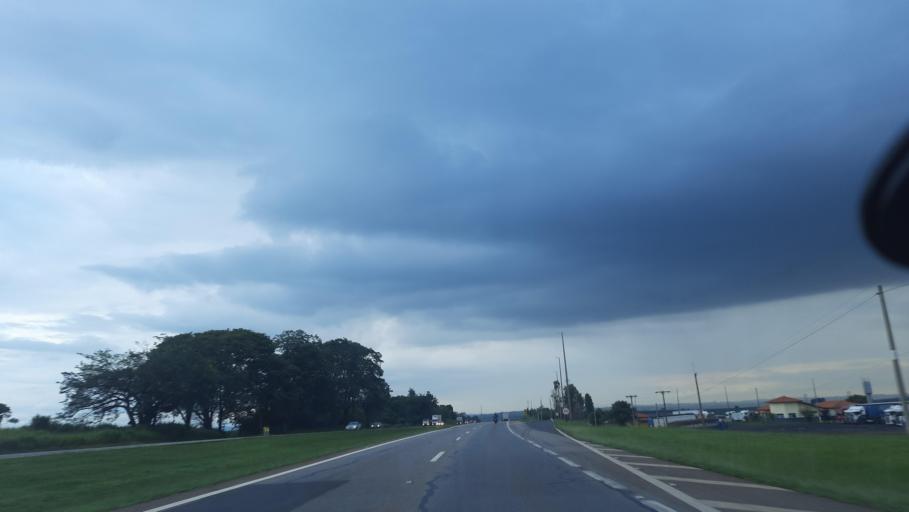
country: BR
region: Sao Paulo
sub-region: Mogi-Mirim
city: Mogi Mirim
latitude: -22.5243
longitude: -46.9919
